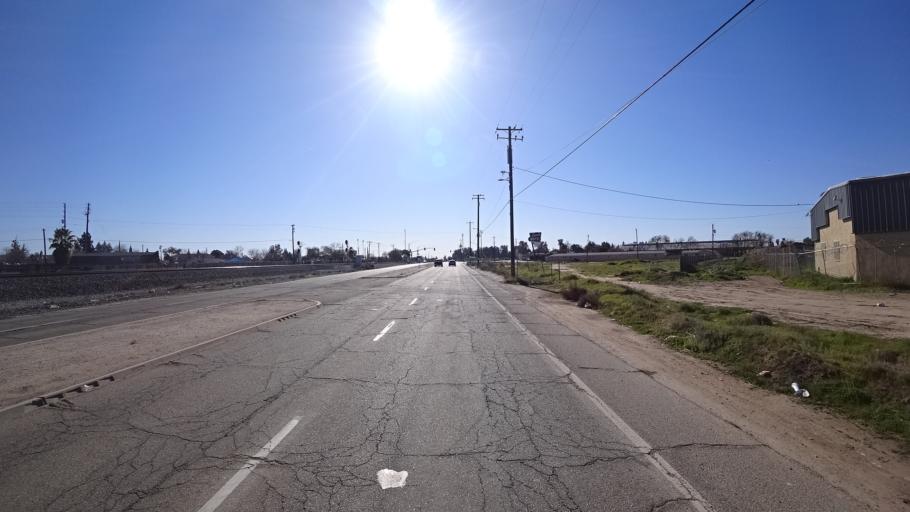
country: US
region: California
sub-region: Fresno County
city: West Park
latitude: 36.7633
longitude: -119.8282
